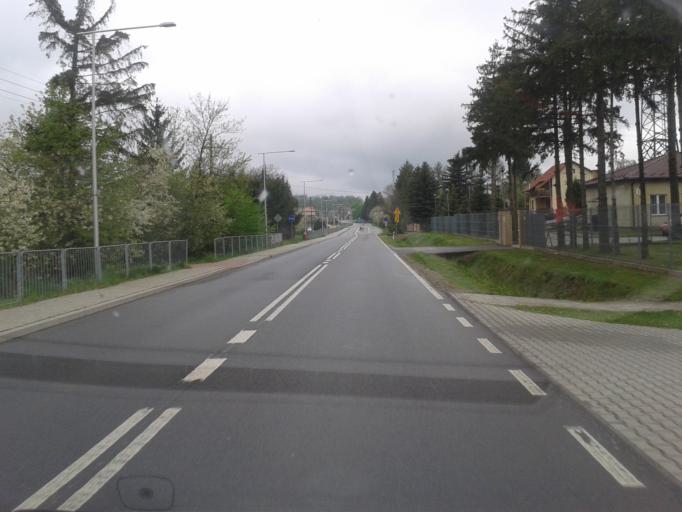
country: PL
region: Lublin Voivodeship
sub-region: Powiat hrubieszowski
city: Dolhobyczow
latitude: 50.5857
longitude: 24.0426
